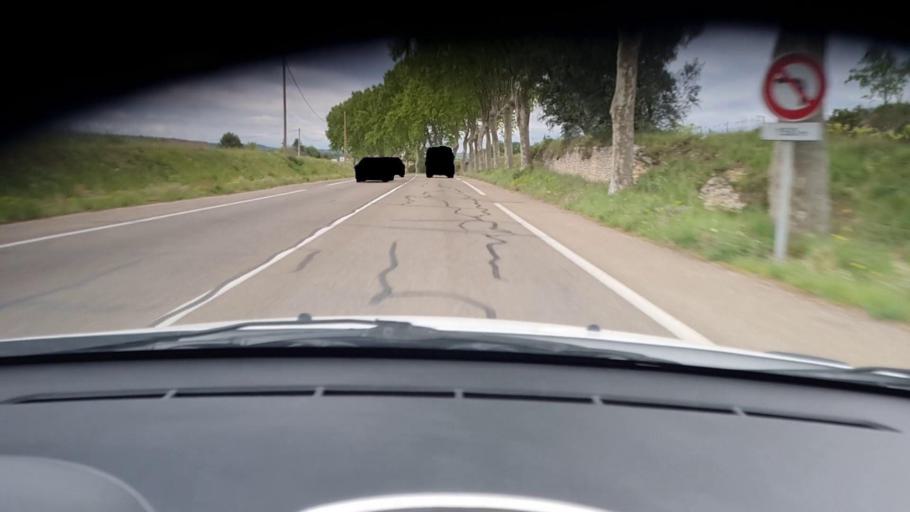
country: FR
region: Languedoc-Roussillon
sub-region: Departement du Gard
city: Uzes
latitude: 43.9857
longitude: 4.4570
